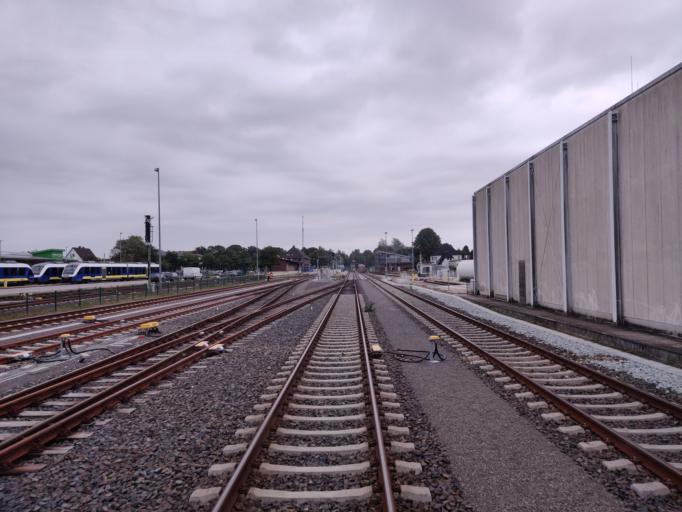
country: DE
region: Lower Saxony
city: Bremervorde
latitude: 53.4840
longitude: 9.1370
